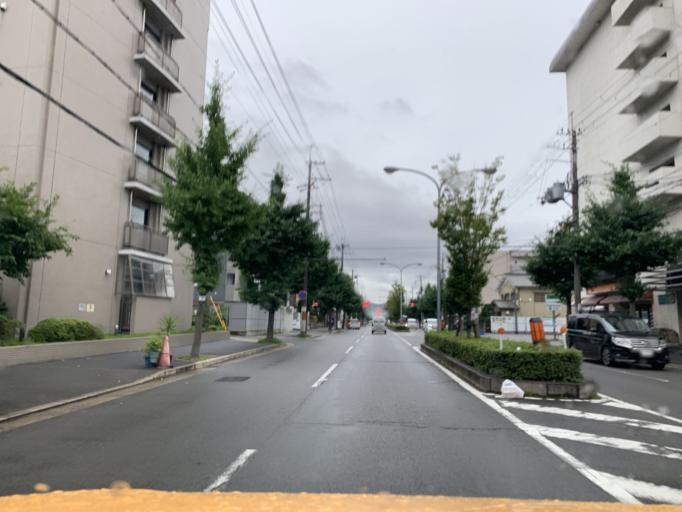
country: JP
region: Kyoto
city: Kyoto
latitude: 35.0109
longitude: 135.7228
